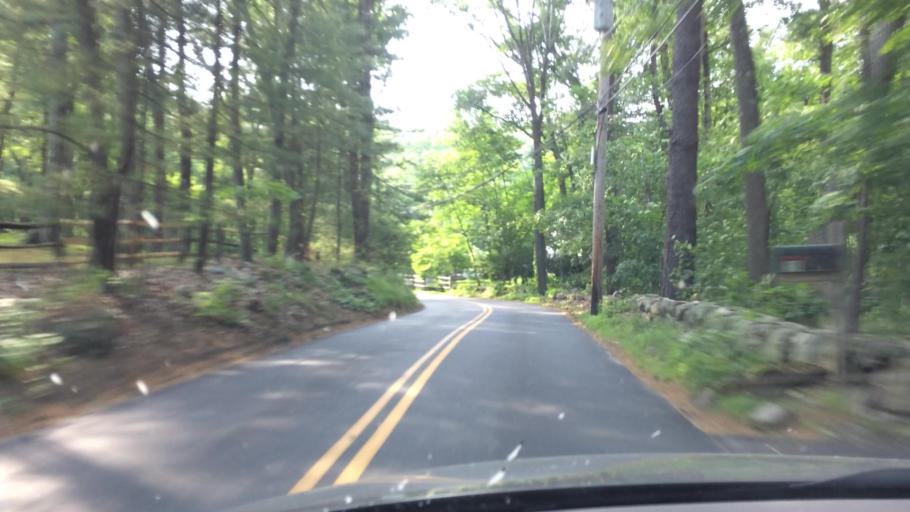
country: US
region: Massachusetts
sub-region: Middlesex County
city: Weston
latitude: 42.3837
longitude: -71.3249
